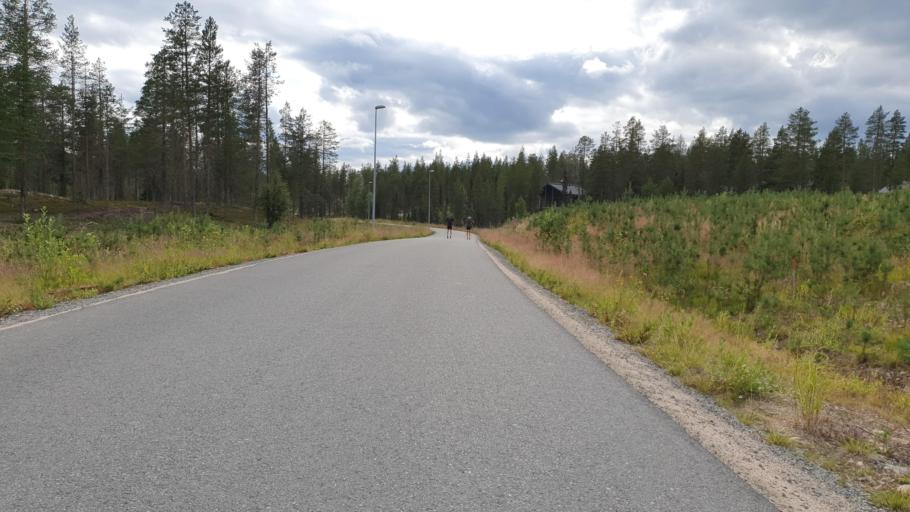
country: FI
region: Lapland
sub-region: Tunturi-Lappi
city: Kolari
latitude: 67.5963
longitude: 24.1364
